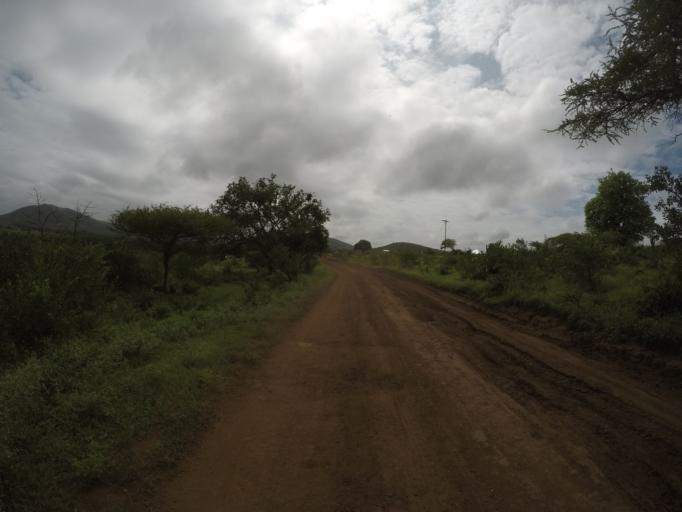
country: ZA
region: KwaZulu-Natal
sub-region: uThungulu District Municipality
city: Empangeni
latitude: -28.6219
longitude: 31.8702
